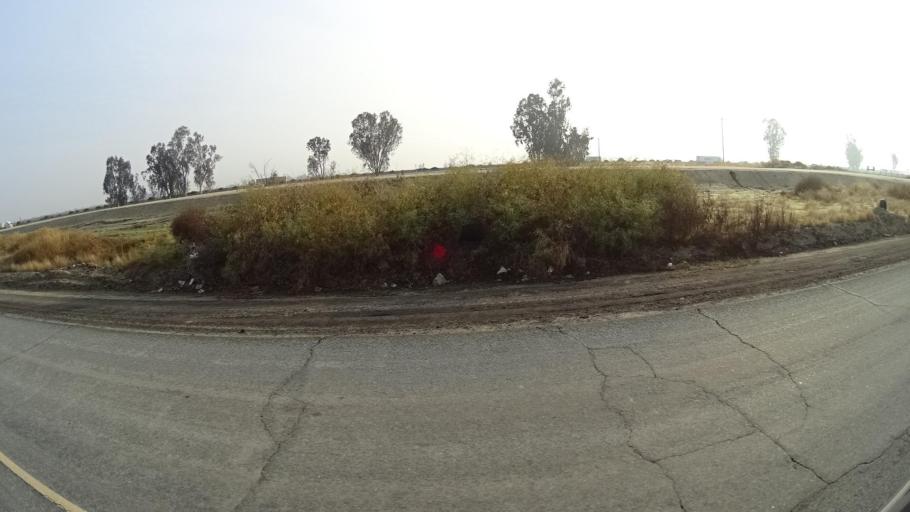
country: US
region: California
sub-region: Kern County
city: Greenfield
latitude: 35.2527
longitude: -119.0213
